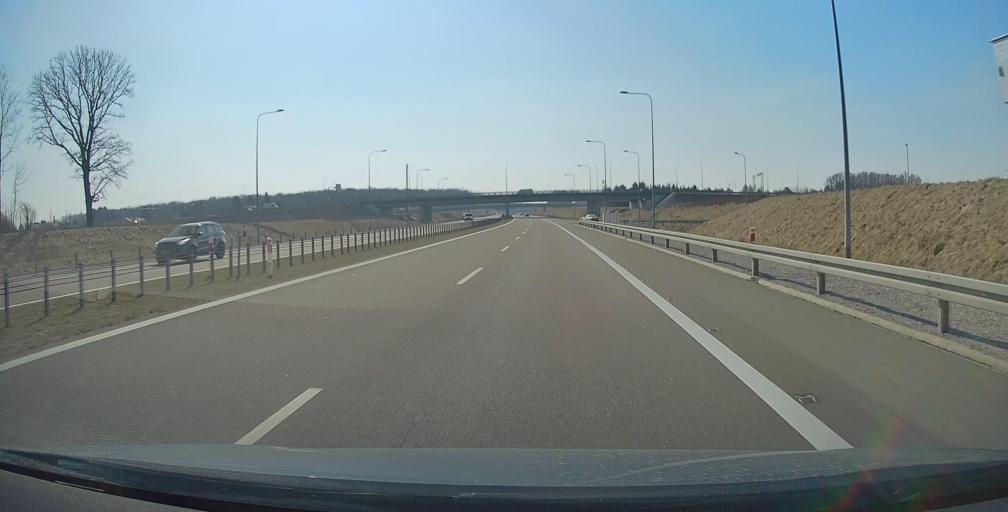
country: PL
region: Lublin Voivodeship
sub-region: Powiat lubelski
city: Kozubszczyzna
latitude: 51.2147
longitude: 22.4414
